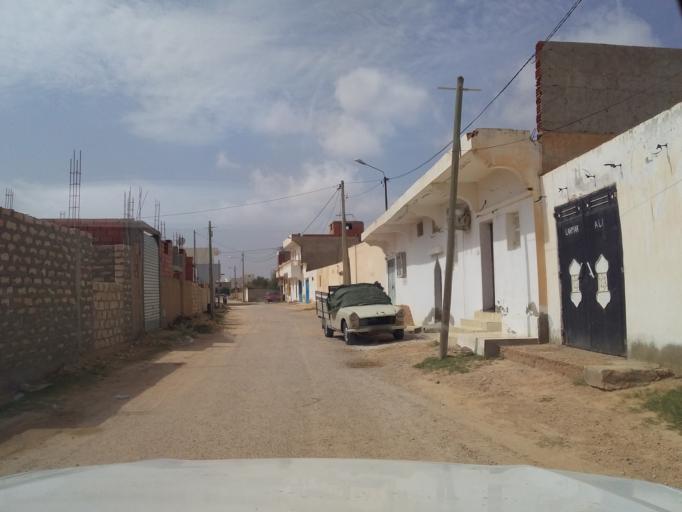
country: TN
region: Qabis
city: Gabes
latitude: 33.6159
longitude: 10.2936
